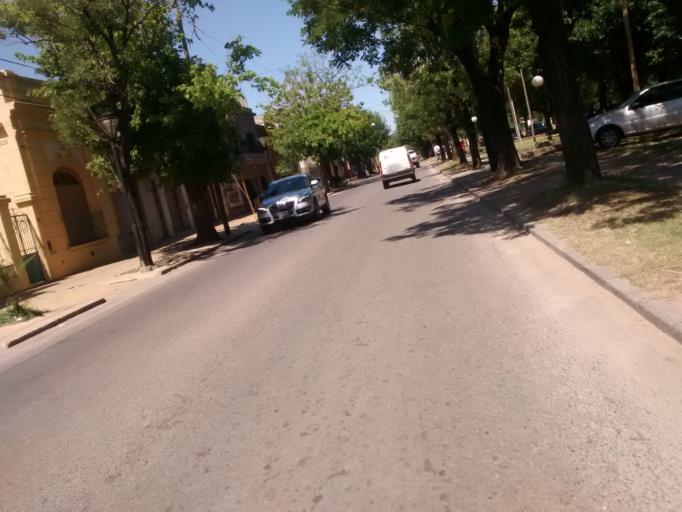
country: AR
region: Buenos Aires
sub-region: Partido de La Plata
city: La Plata
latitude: -34.8920
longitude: -57.9671
